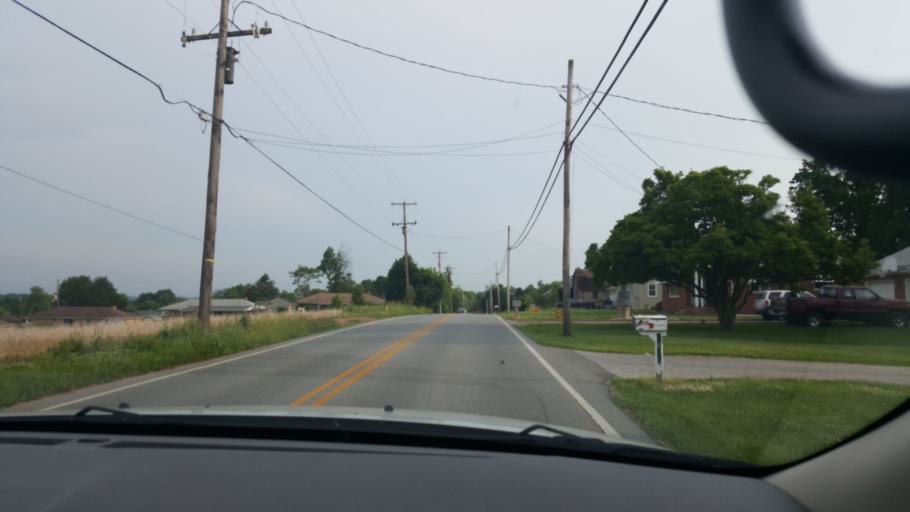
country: US
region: Pennsylvania
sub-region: York County
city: Weigelstown
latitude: 39.9967
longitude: -76.8118
